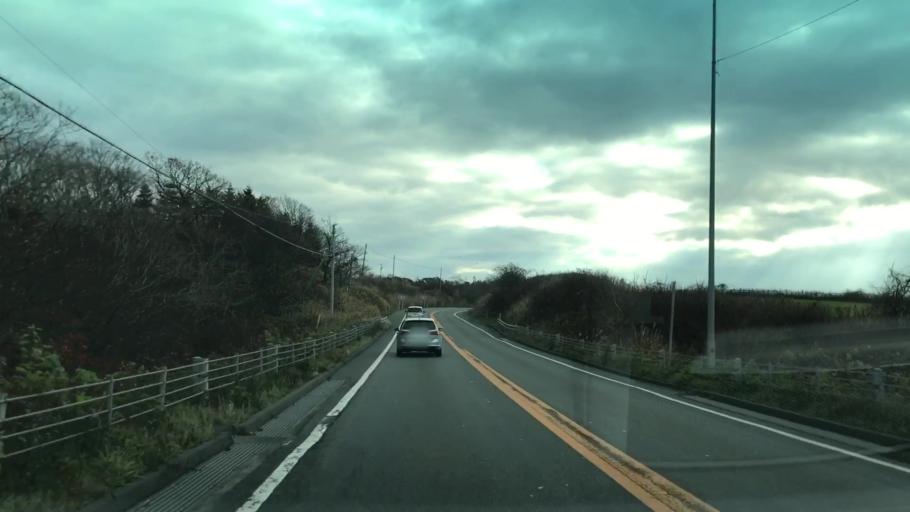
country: JP
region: Hokkaido
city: Shizunai-furukawacho
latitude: 42.4137
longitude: 142.2393
